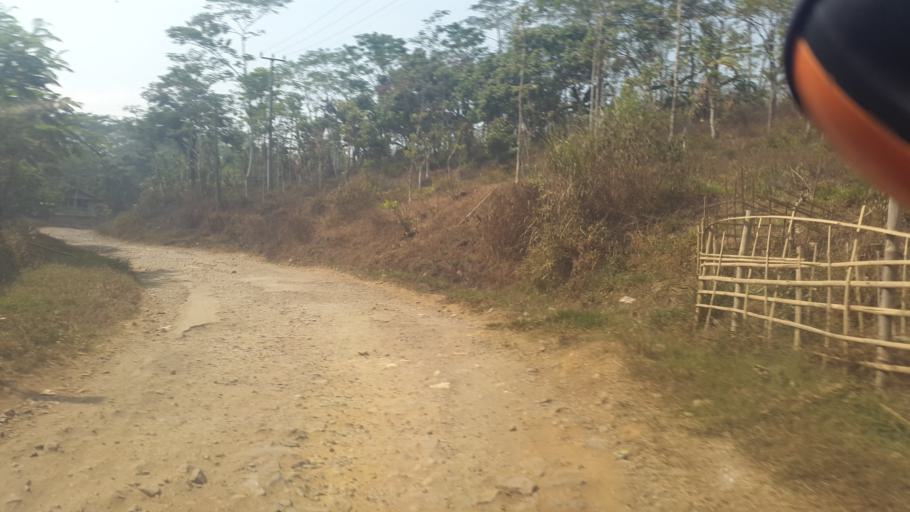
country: ID
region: West Java
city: Pasirlaja
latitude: -7.0547
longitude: 106.8713
